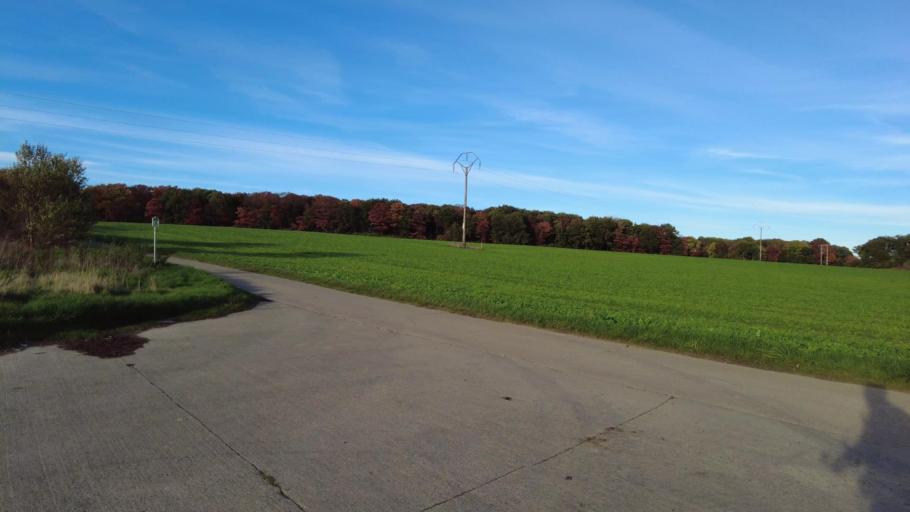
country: BE
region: Flanders
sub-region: Provincie Vlaams-Brabant
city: Hoegaarden
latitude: 50.7313
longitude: 4.9483
